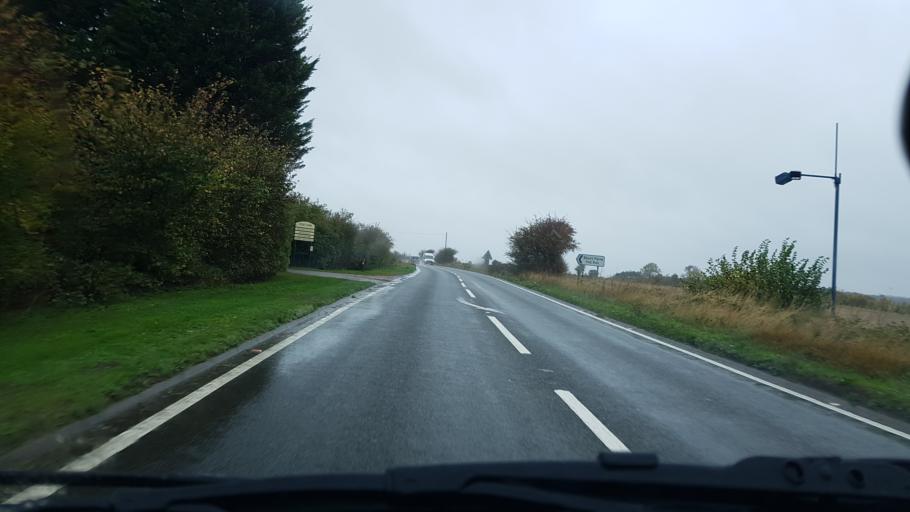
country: GB
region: England
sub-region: Oxfordshire
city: Carterton
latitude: 51.7941
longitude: -1.6014
